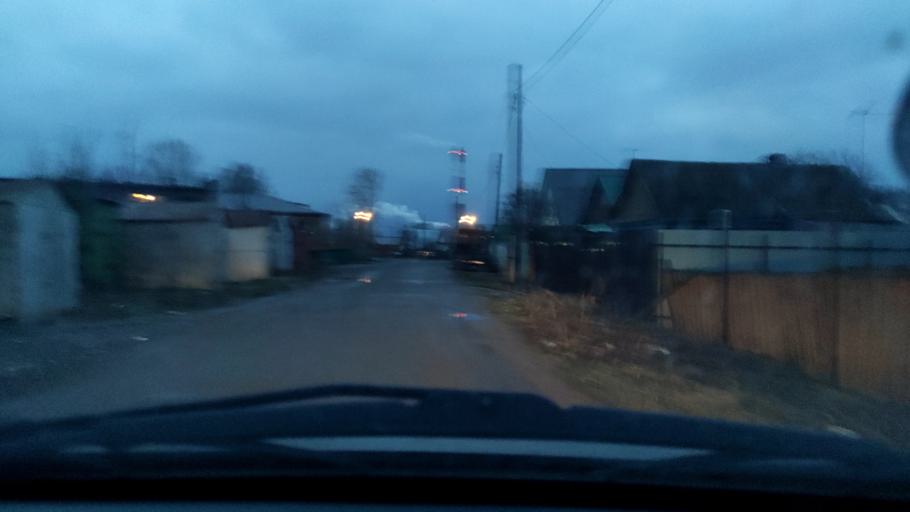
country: RU
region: Bashkortostan
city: Iglino
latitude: 54.7632
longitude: 56.2363
